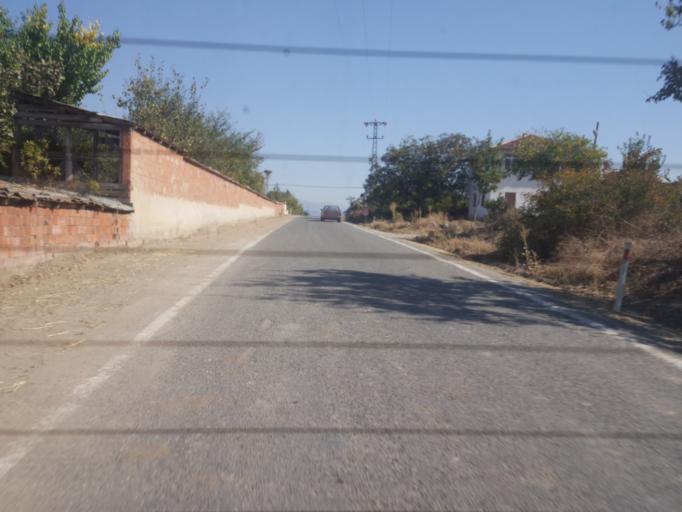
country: TR
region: Kastamonu
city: Tosya
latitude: 40.9902
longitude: 34.1122
